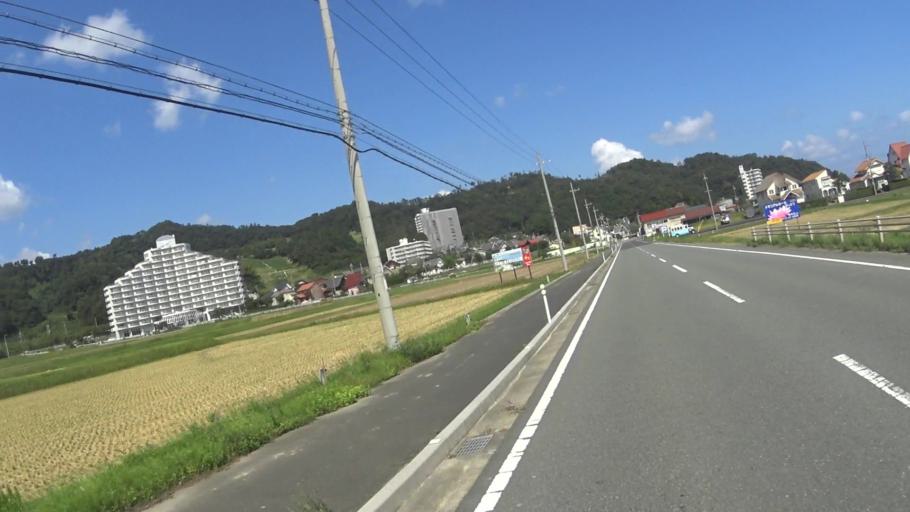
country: JP
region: Kyoto
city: Miyazu
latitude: 35.6134
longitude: 135.2304
